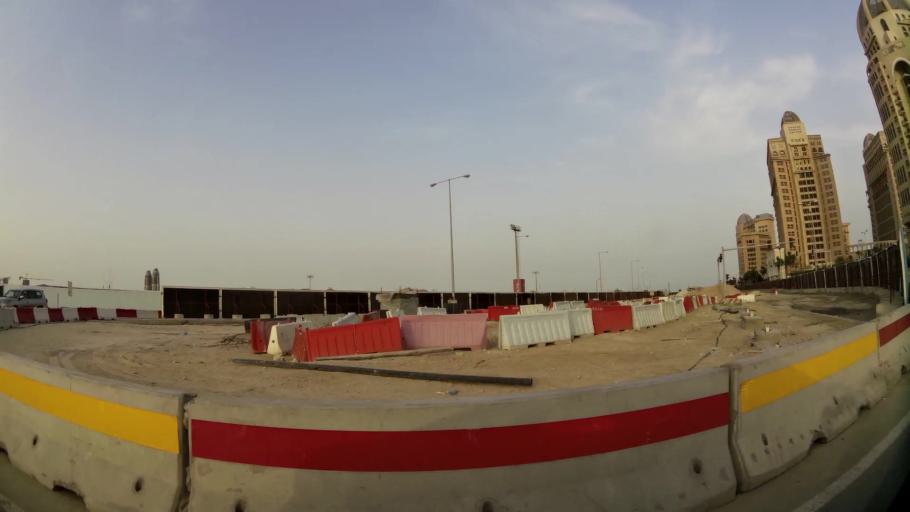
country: QA
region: Baladiyat ad Dawhah
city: Doha
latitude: 25.3511
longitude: 51.5254
